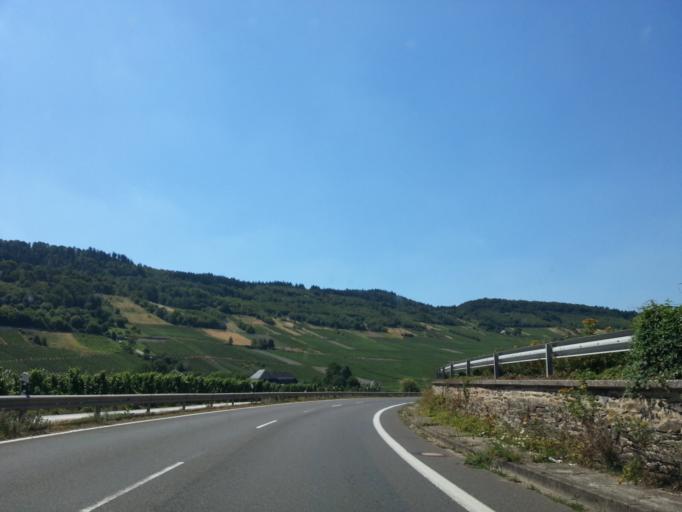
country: DE
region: Rheinland-Pfalz
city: Trittenheim
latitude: 49.8175
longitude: 6.8963
